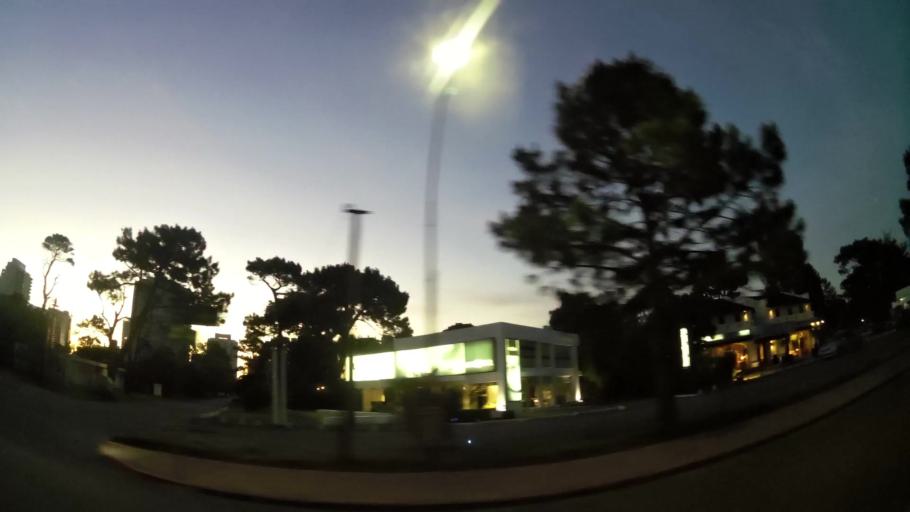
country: UY
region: Maldonado
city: Punta del Este
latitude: -34.9468
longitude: -54.9333
